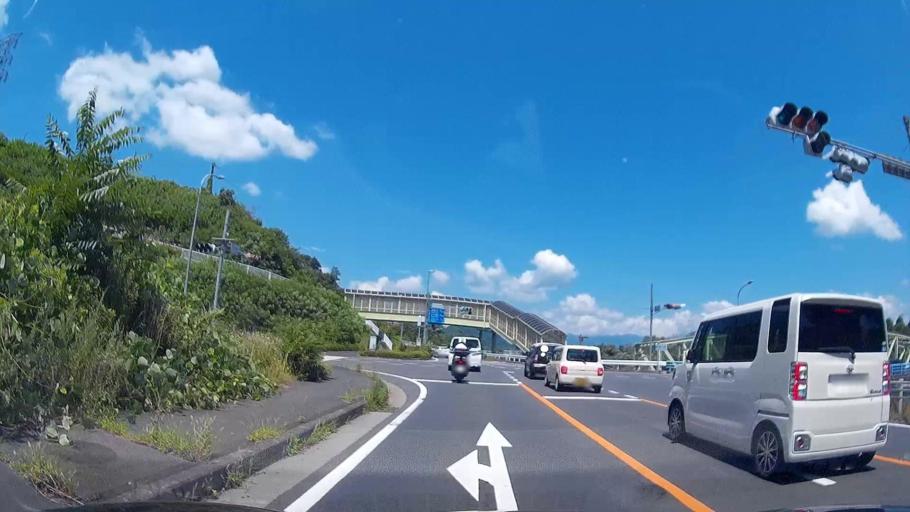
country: JP
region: Gunma
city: Numata
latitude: 36.6316
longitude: 139.0371
